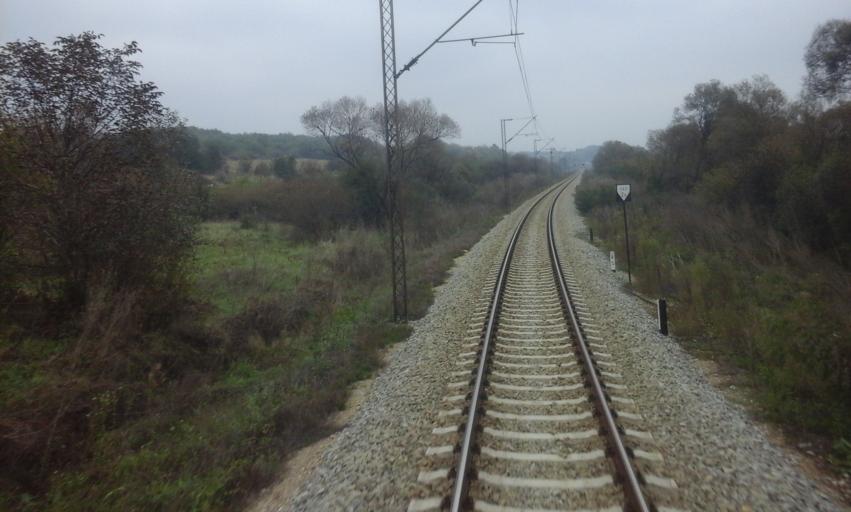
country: RS
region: Central Serbia
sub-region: Belgrade
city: Sopot
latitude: 44.4991
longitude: 20.6456
